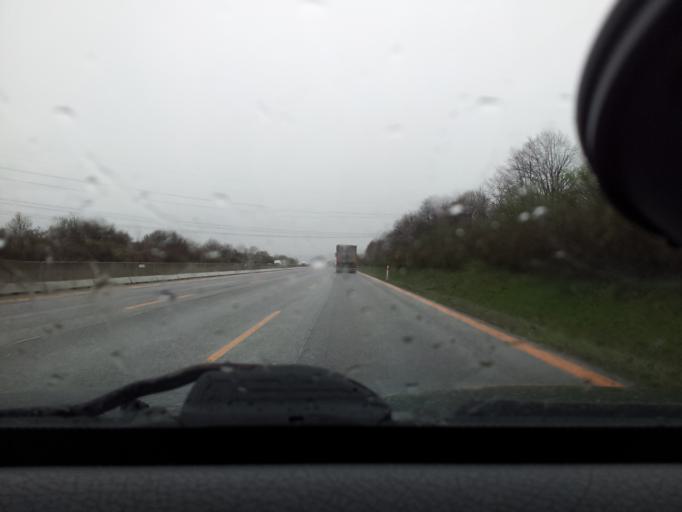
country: SK
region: Bratislavsky
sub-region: Okres Pezinok
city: Pezinok
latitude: 48.2150
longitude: 17.2893
